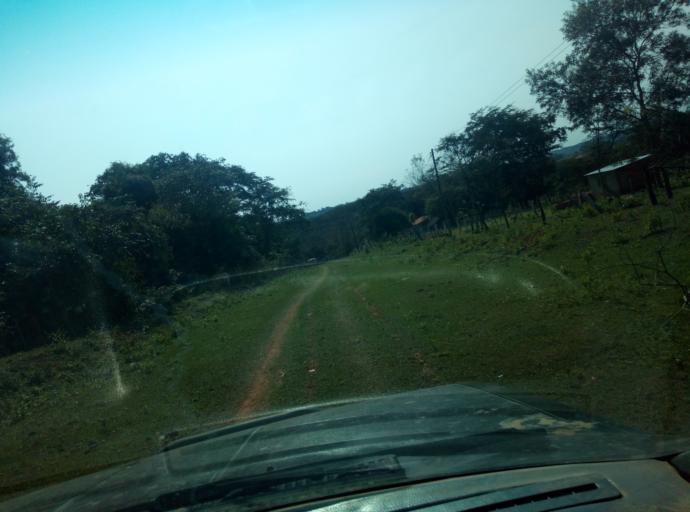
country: PY
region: Caaguazu
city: Carayao
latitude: -25.3025
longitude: -56.3231
